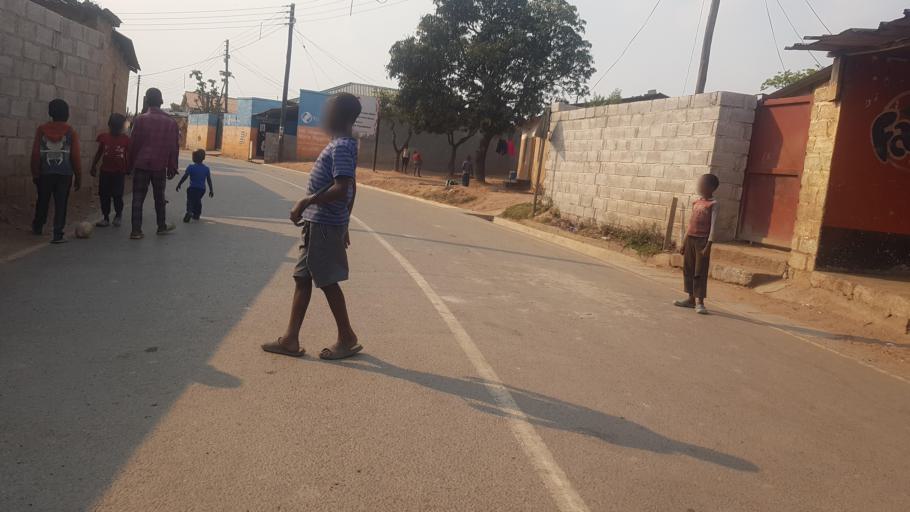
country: ZM
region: Lusaka
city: Lusaka
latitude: -15.4450
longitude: 28.3865
